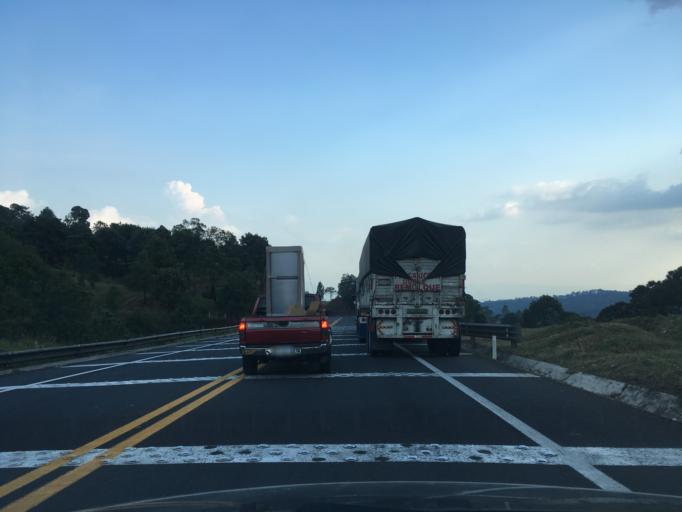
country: MX
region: Michoacan
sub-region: Uruapan
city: Toreo Bajo (El Toreo Bajo)
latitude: 19.4179
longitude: -101.9836
